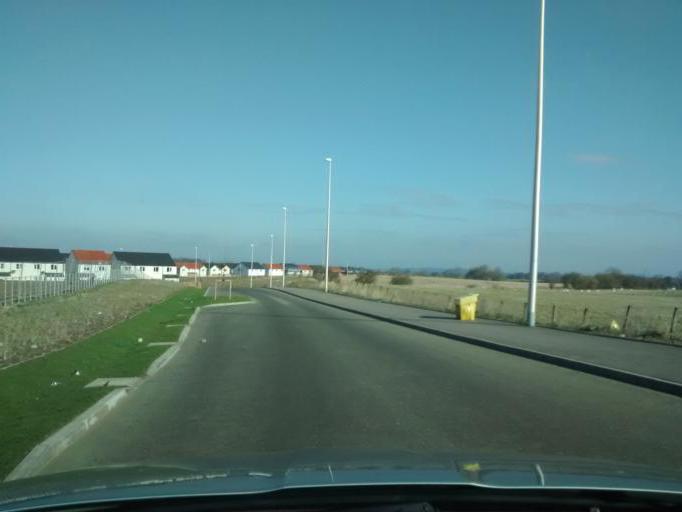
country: GB
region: Scotland
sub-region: West Lothian
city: East Calder
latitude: 55.8991
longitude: -3.4502
